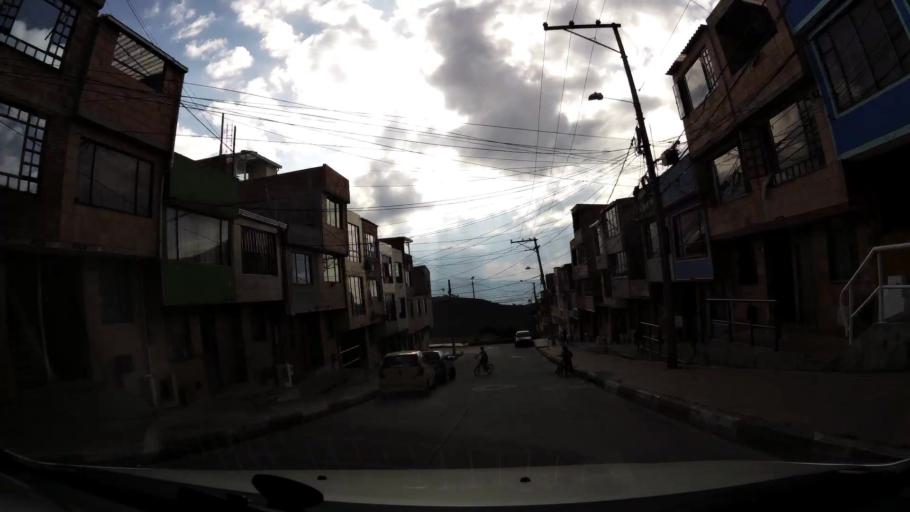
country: CO
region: Bogota D.C.
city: Bogota
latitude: 4.5386
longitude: -74.0917
